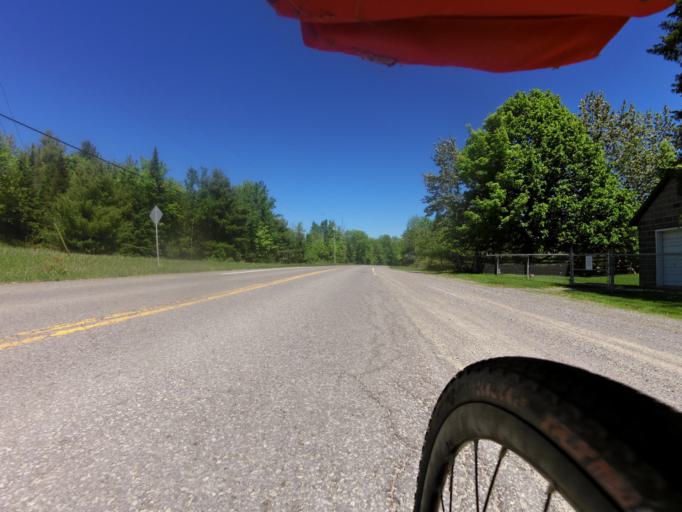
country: CA
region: Ontario
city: Carleton Place
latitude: 45.1872
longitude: -76.3378
